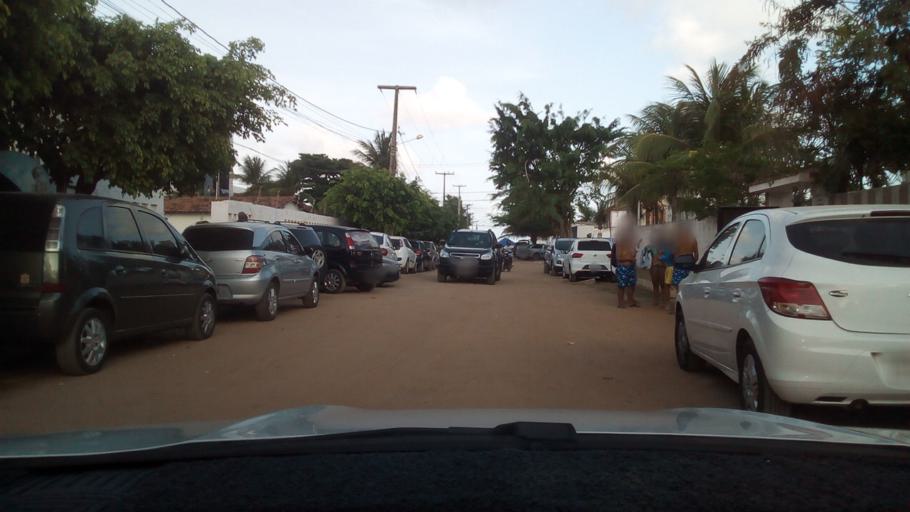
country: BR
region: Paraiba
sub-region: Cabedelo
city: Cabedelo
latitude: -7.0062
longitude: -34.8280
